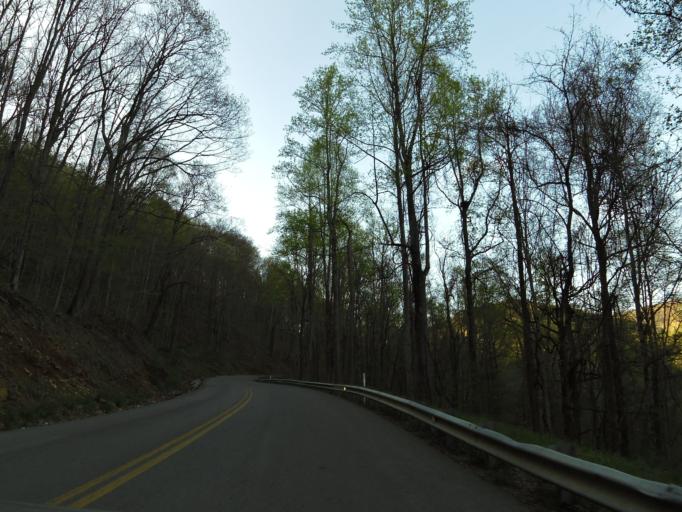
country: US
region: Kentucky
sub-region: Bell County
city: Middlesboro
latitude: 36.6340
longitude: -83.8513
